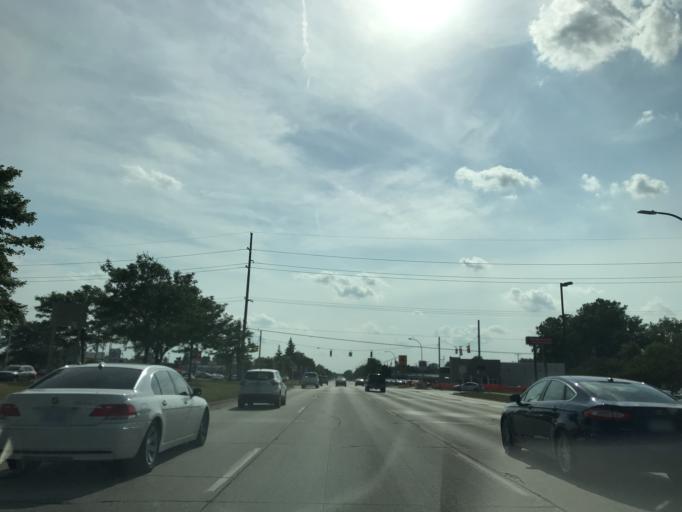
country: US
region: Michigan
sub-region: Wayne County
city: Wayne
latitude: 42.2836
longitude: -83.3620
